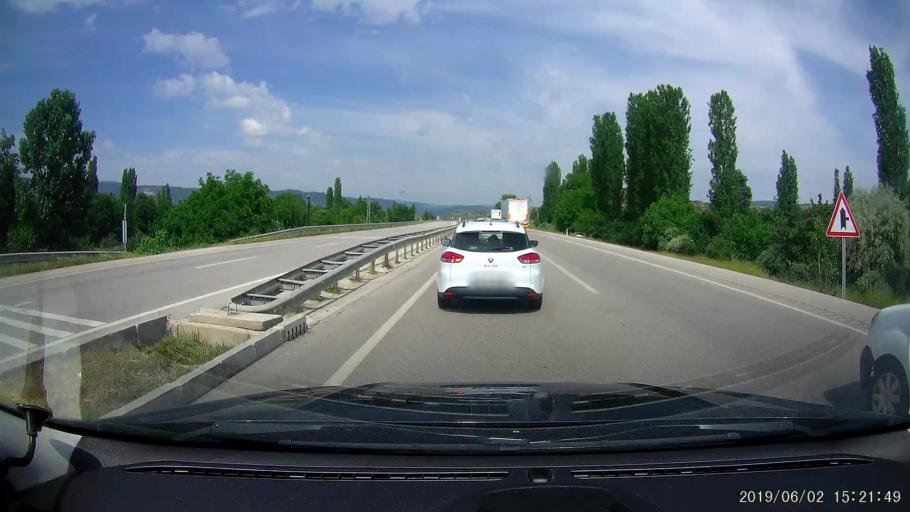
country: TR
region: Corum
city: Osmancik
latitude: 40.9792
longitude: 34.9445
